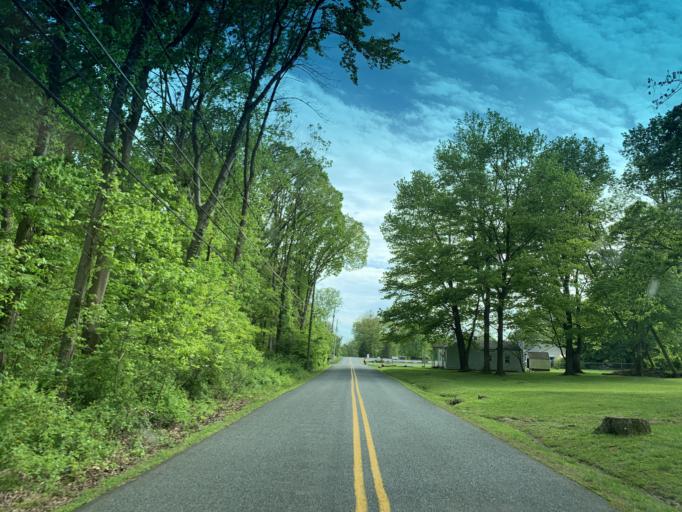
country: US
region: Maryland
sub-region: Harford County
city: Aberdeen
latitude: 39.6495
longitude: -76.2290
